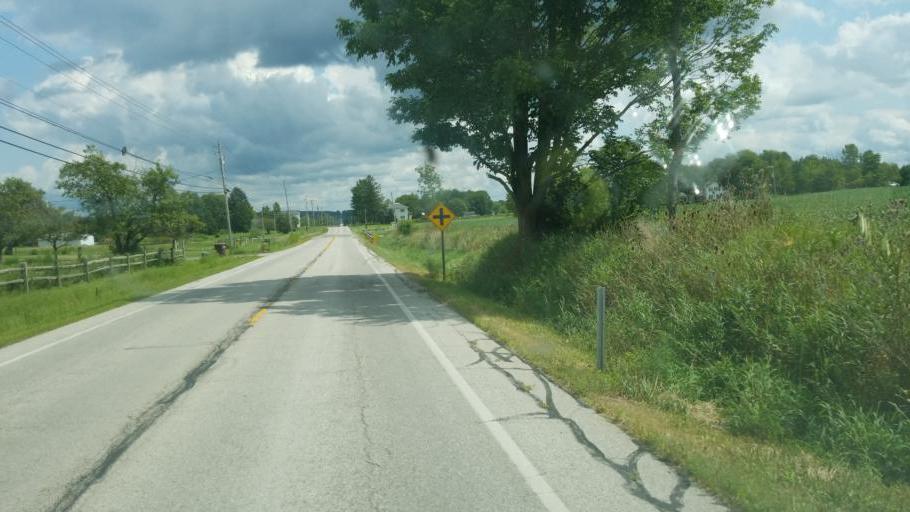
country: US
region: Ohio
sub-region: Ashtabula County
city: Andover
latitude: 41.6069
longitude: -80.6515
